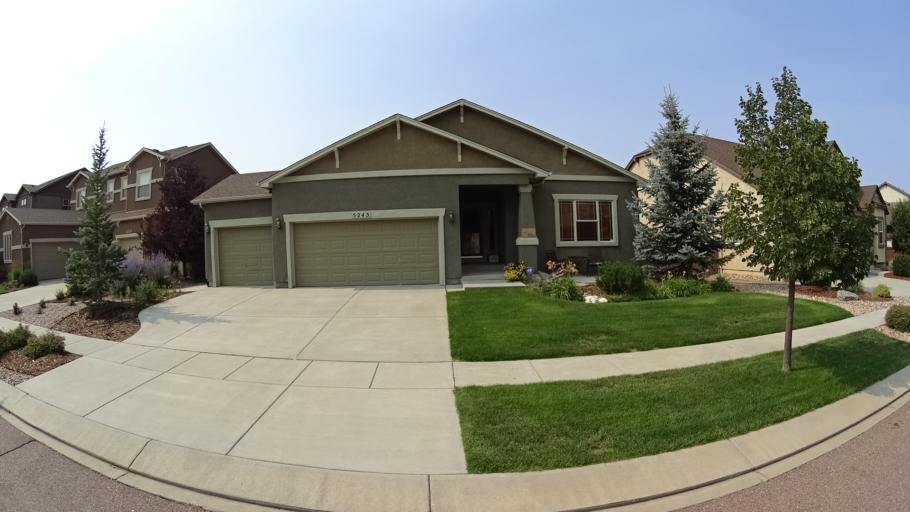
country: US
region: Colorado
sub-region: El Paso County
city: Black Forest
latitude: 38.9695
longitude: -104.7301
